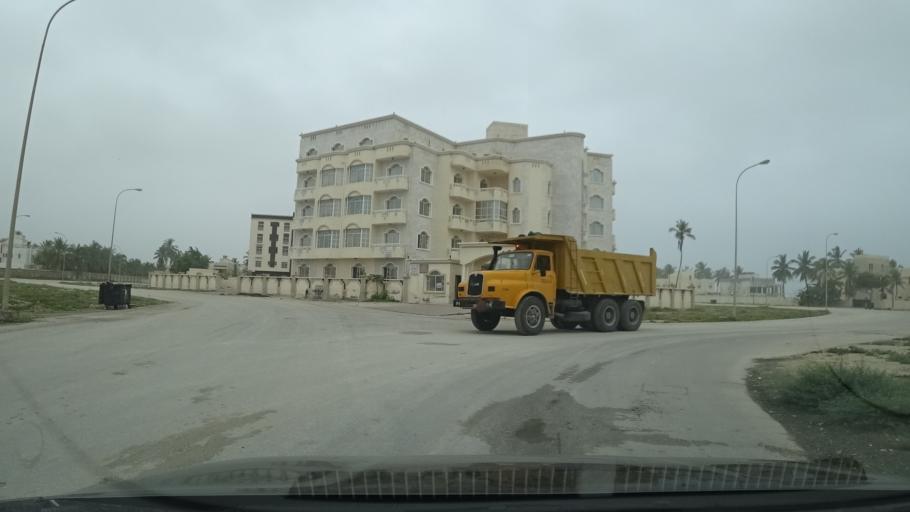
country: OM
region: Zufar
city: Salalah
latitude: 17.0099
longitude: 54.1550
